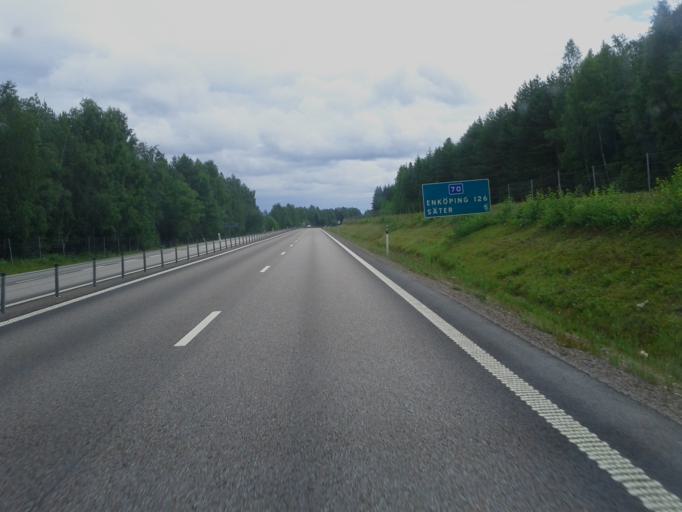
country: SE
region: Dalarna
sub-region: Saters Kommun
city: Saeter
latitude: 60.3797
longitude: 15.6793
